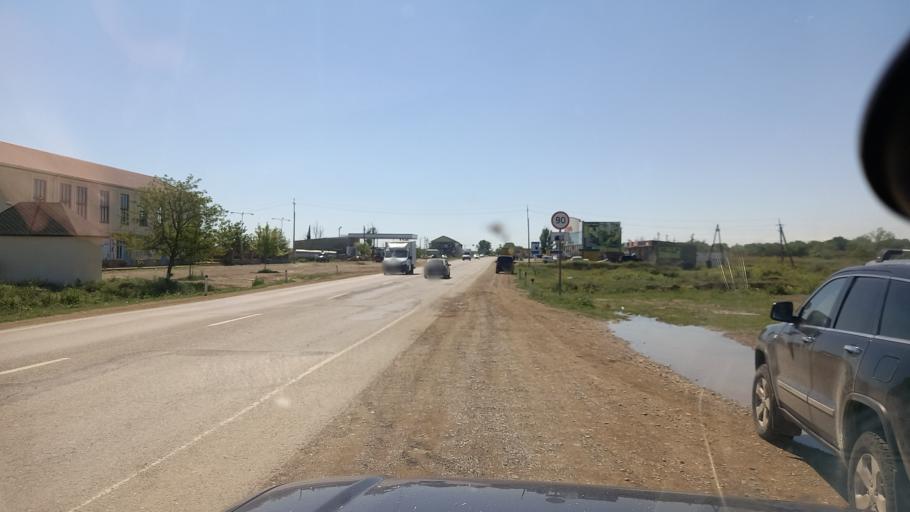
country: RU
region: Dagestan
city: Belidzhi
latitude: 41.8614
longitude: 48.3662
